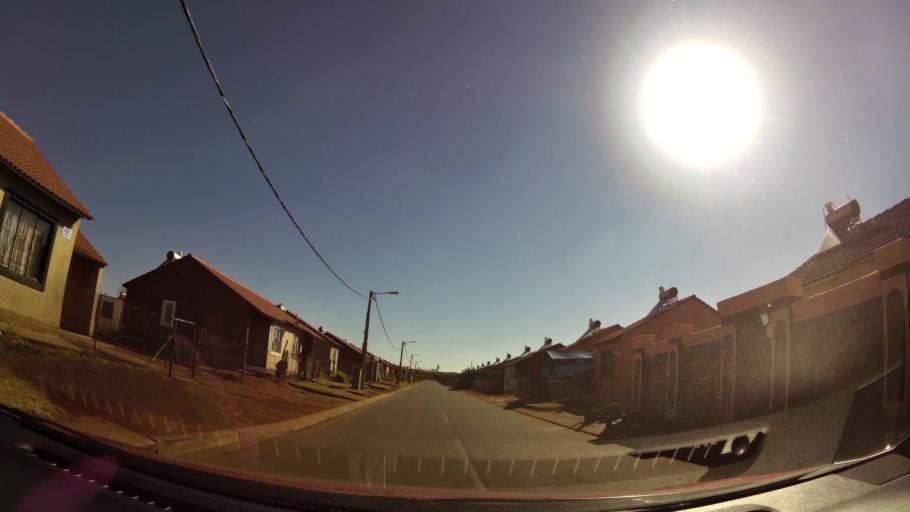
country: ZA
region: Gauteng
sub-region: City of Johannesburg Metropolitan Municipality
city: Soweto
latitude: -26.2408
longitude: 27.7983
